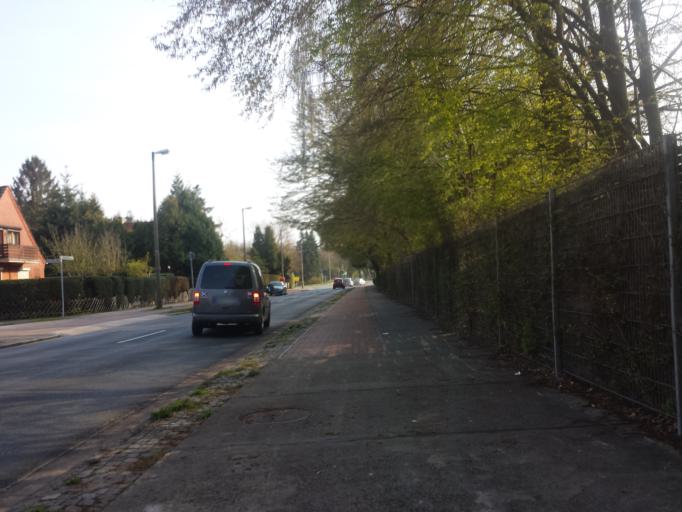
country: DE
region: Lower Saxony
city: Lilienthal
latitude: 53.0730
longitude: 8.9020
